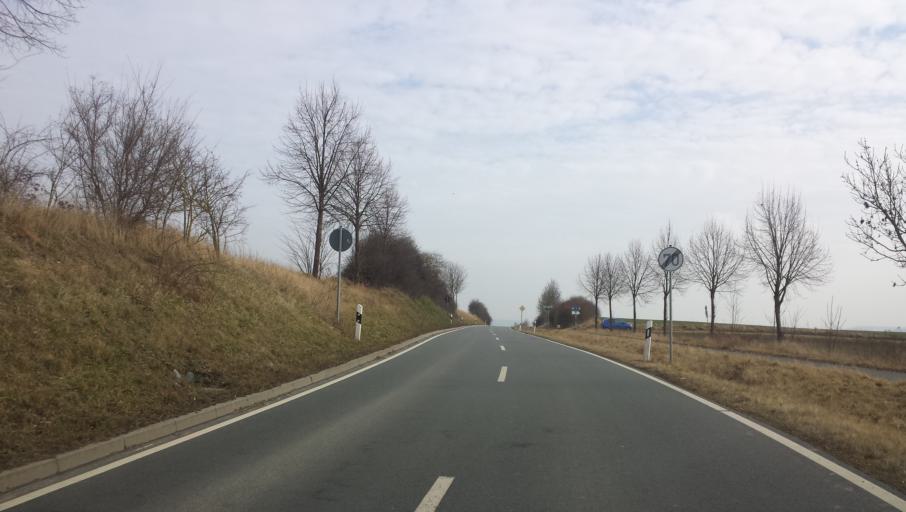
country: DE
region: Hesse
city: Reinheim
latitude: 49.8510
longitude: 8.8602
